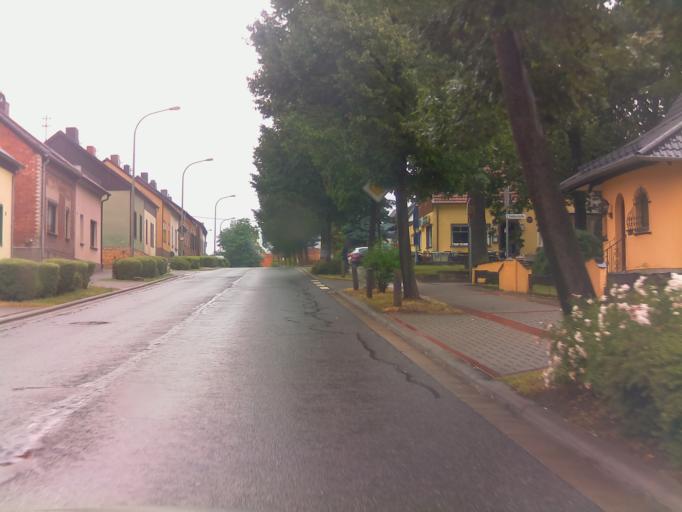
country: DE
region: Saarland
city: Friedrichsthal
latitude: 49.3328
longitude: 7.0871
